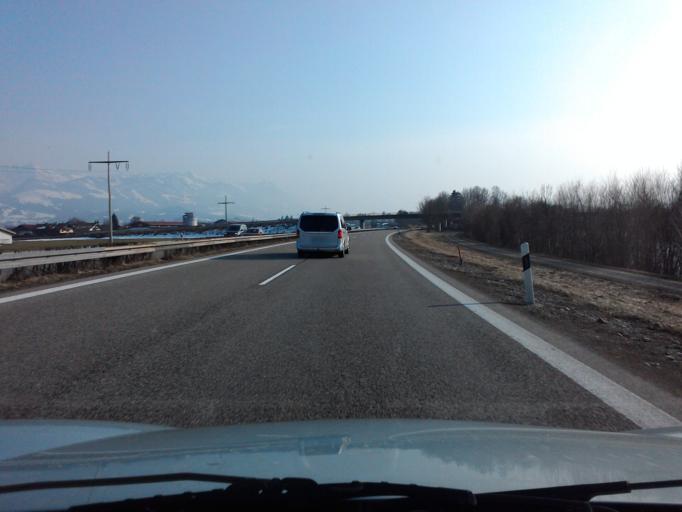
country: DE
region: Bavaria
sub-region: Swabia
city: Blaichach
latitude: 47.5429
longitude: 10.2674
